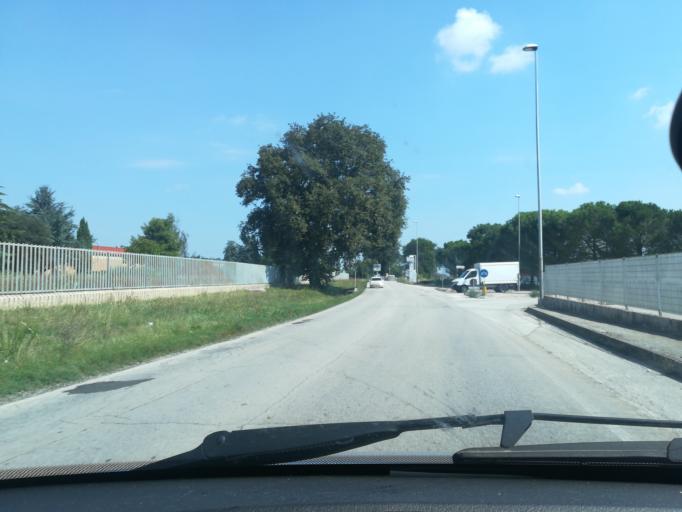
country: IT
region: The Marches
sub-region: Provincia di Macerata
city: Tolentino
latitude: 43.2222
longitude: 13.3314
